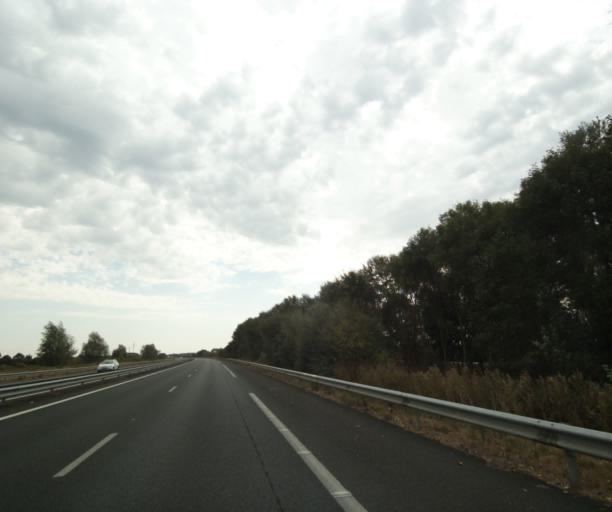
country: FR
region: Poitou-Charentes
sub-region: Departement de la Charente-Maritime
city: Breuil-Magne
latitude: 45.9585
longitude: -0.9420
